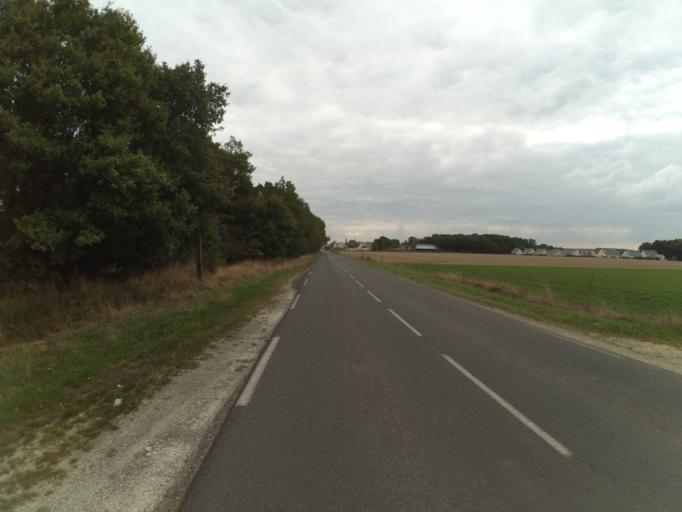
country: FR
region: Centre
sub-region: Departement d'Indre-et-Loire
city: Auzouer-en-Touraine
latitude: 47.4903
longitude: 0.9413
